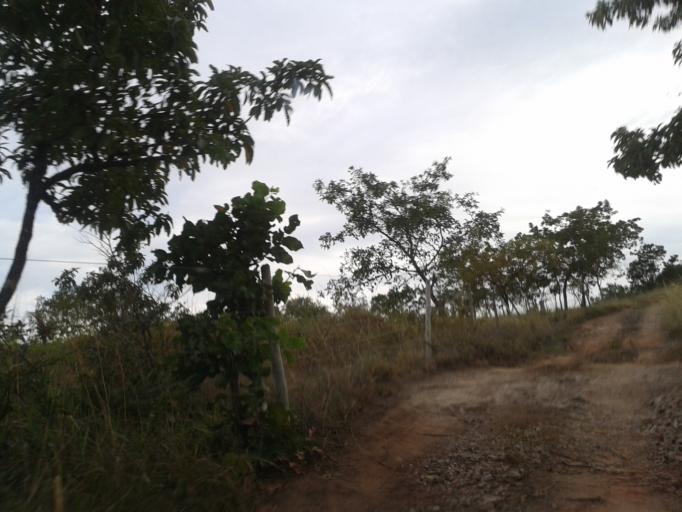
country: BR
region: Minas Gerais
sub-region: Campina Verde
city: Campina Verde
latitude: -19.4175
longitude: -49.6117
